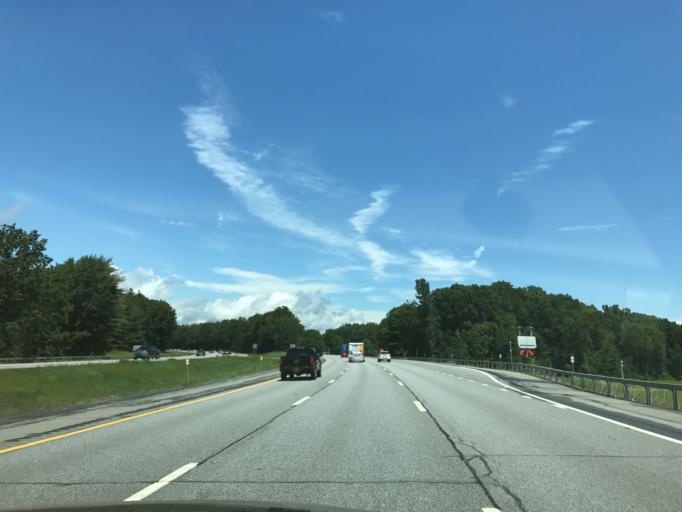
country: US
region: New York
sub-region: Warren County
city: West Glens Falls
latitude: 43.2674
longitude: -73.6745
